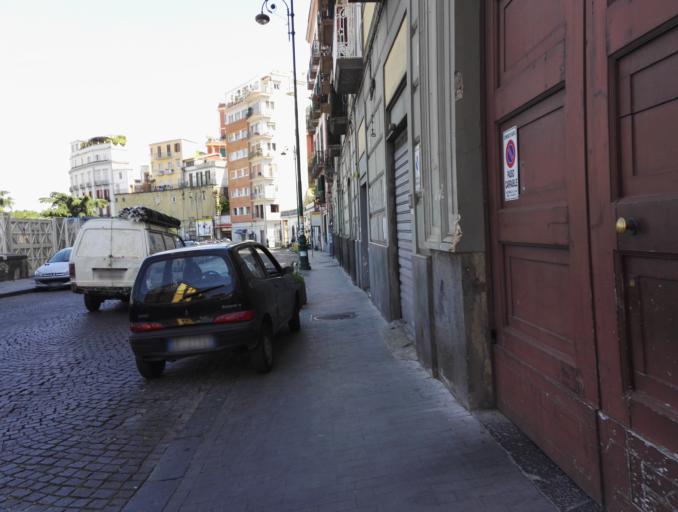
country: IT
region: Campania
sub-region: Provincia di Napoli
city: Napoli
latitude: 40.8469
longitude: 14.2418
